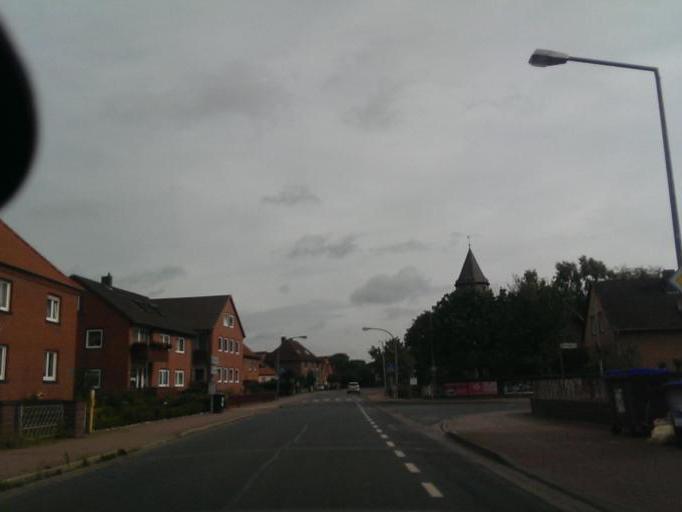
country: DE
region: Lower Saxony
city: Garbsen-Mitte
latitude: 52.4590
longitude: 9.5789
